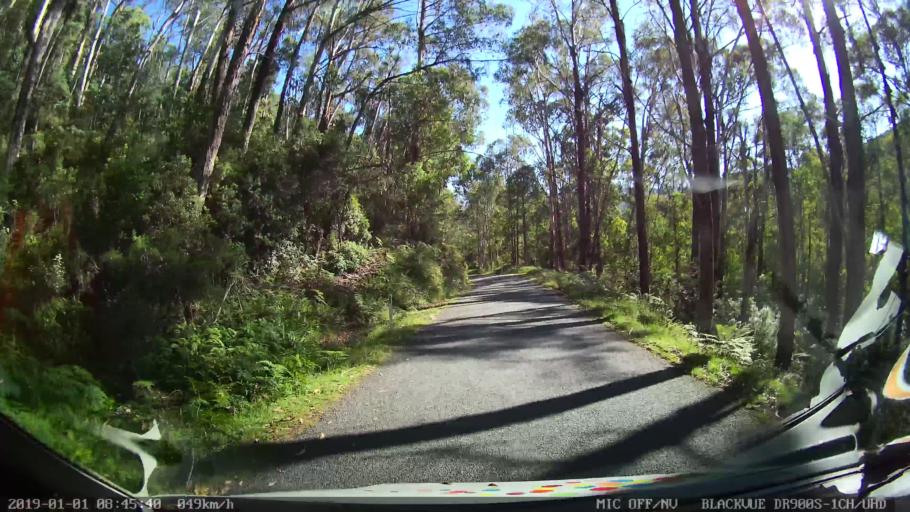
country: AU
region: New South Wales
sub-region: Snowy River
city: Jindabyne
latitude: -36.3041
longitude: 148.1896
